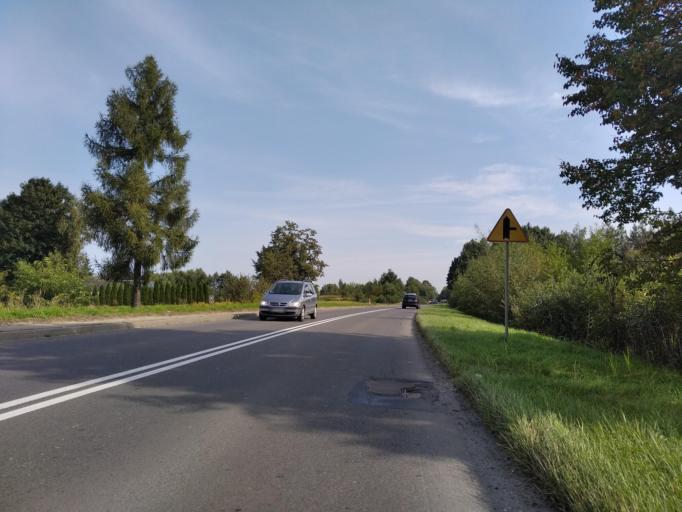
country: PL
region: Subcarpathian Voivodeship
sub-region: Powiat ropczycko-sedziszowski
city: Ostrow
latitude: 50.0830
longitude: 21.5844
